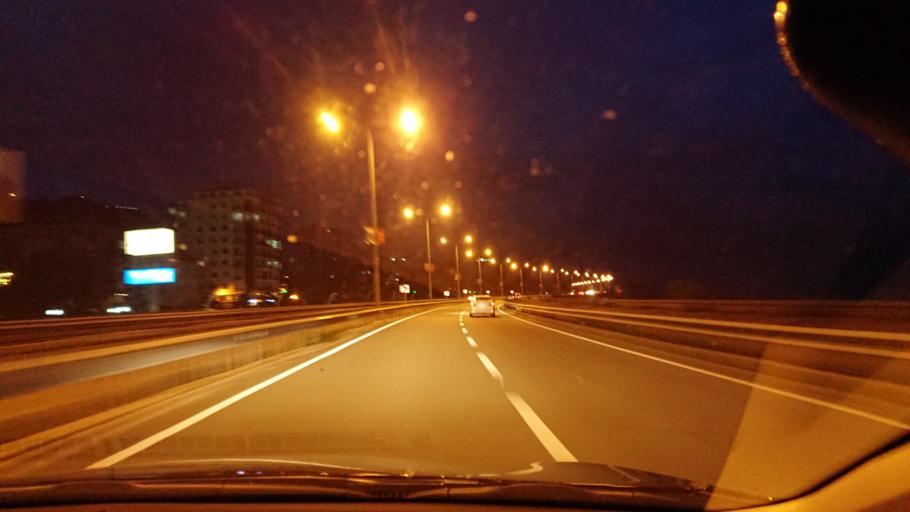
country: TR
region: Rize
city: Gundogdu
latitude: 41.0473
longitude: 40.6011
